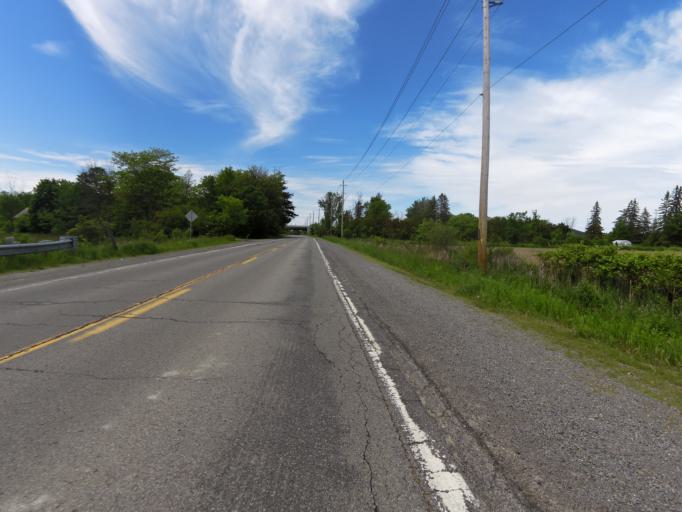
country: CA
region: Ontario
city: Ottawa
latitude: 45.3800
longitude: -75.5823
